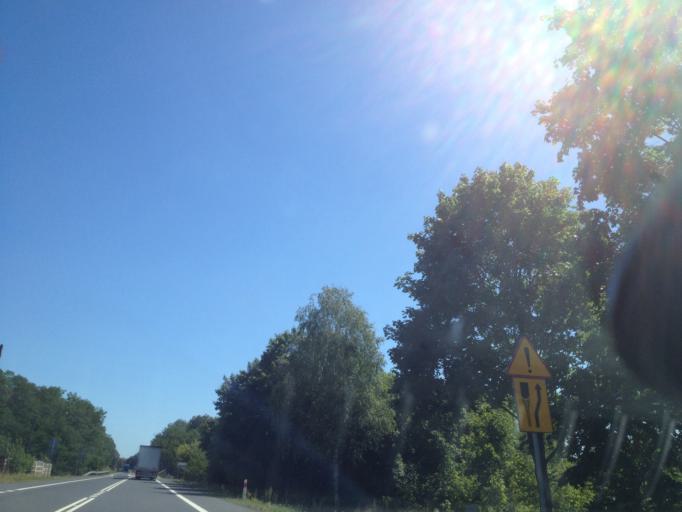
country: PL
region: Lubusz
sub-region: Powiat sulecinski
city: Torzym
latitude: 52.3159
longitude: 15.0492
